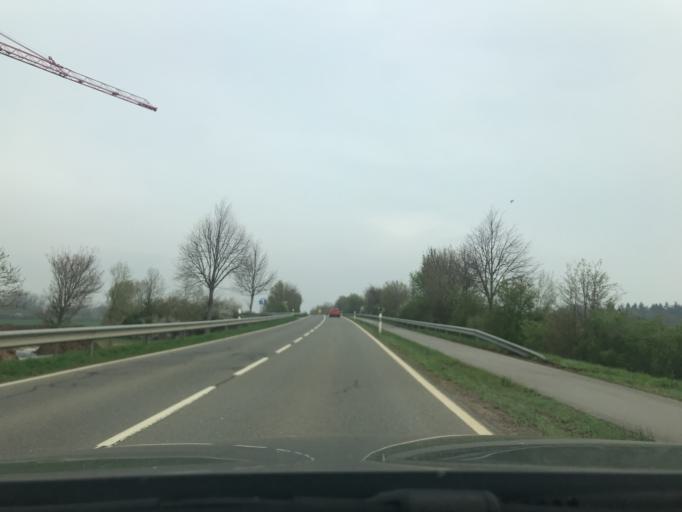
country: DE
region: North Rhine-Westphalia
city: Geldern
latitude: 51.4956
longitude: 6.3198
